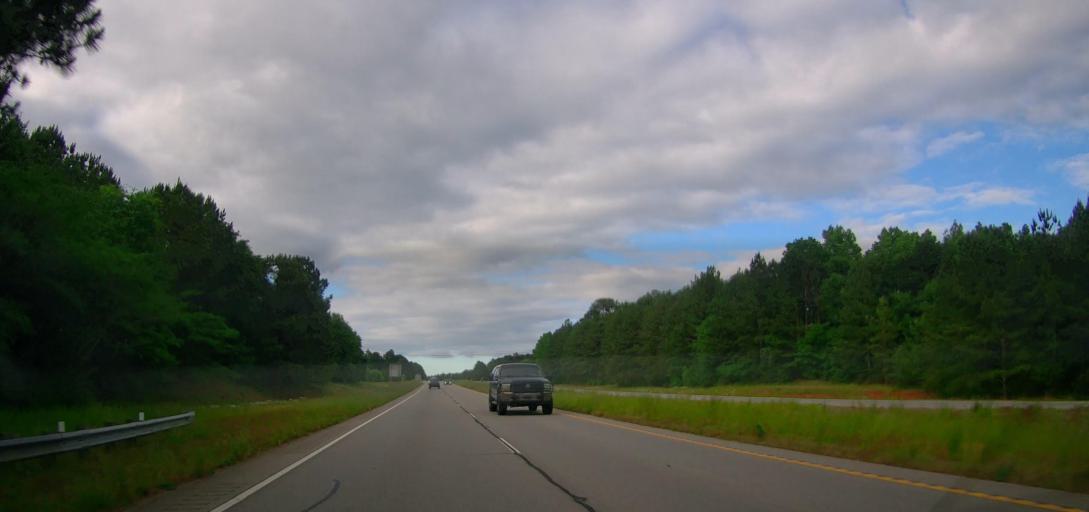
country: US
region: Georgia
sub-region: Oconee County
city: Watkinsville
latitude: 33.8741
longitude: -83.4196
